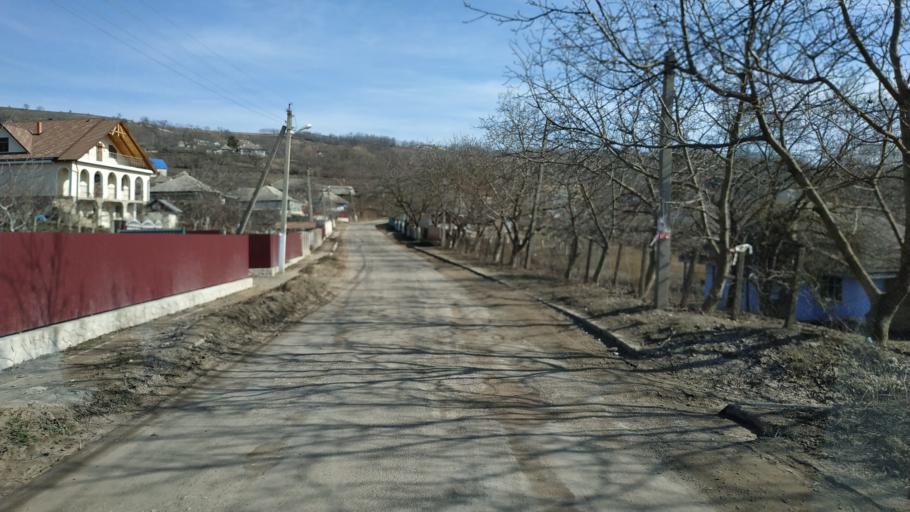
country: MD
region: Nisporeni
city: Nisporeni
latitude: 47.2228
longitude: 28.0410
